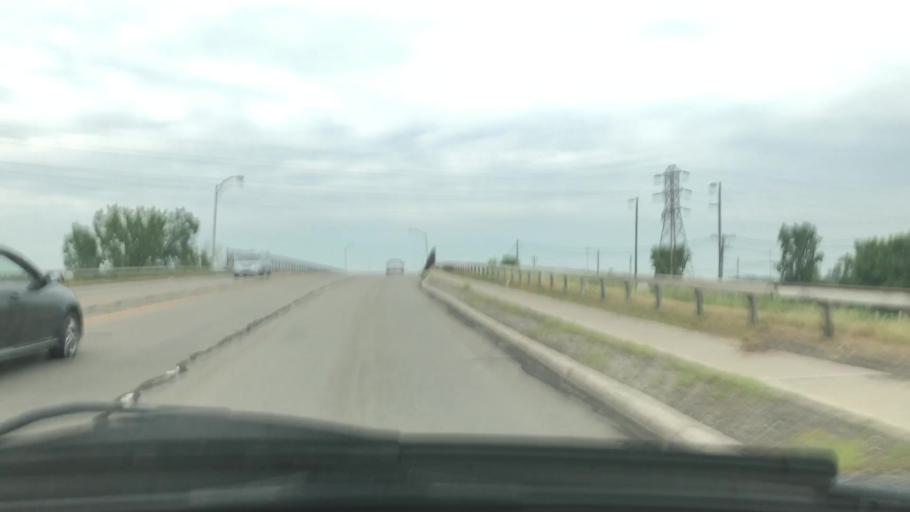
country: US
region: New York
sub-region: Erie County
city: Sloan
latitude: 42.8873
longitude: -78.7847
